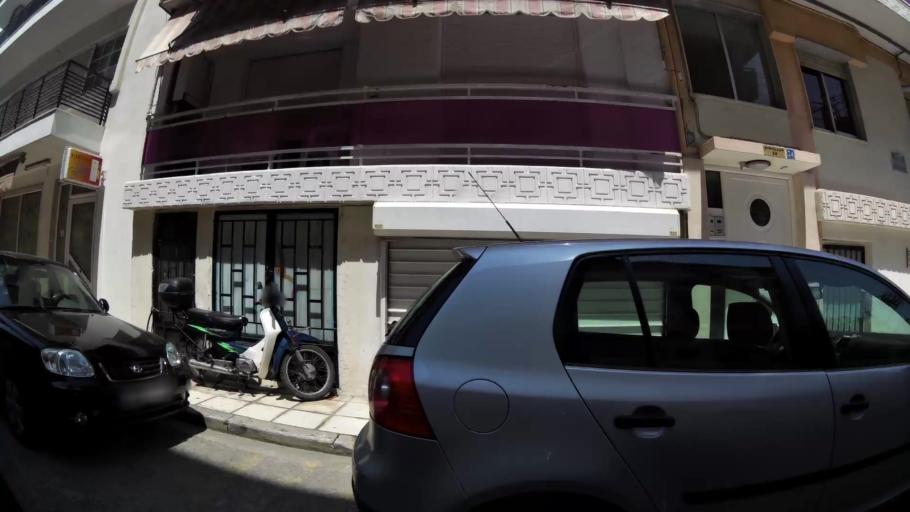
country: GR
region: Central Macedonia
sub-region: Nomos Thessalonikis
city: Ampelokipoi
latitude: 40.6560
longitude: 22.9289
